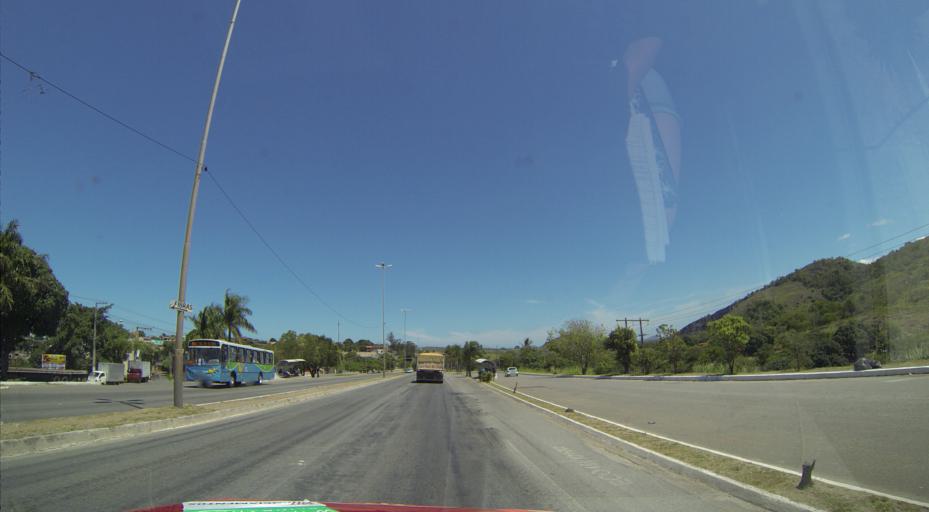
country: BR
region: Espirito Santo
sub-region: Serra
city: Serra
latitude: -20.1587
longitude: -40.2764
